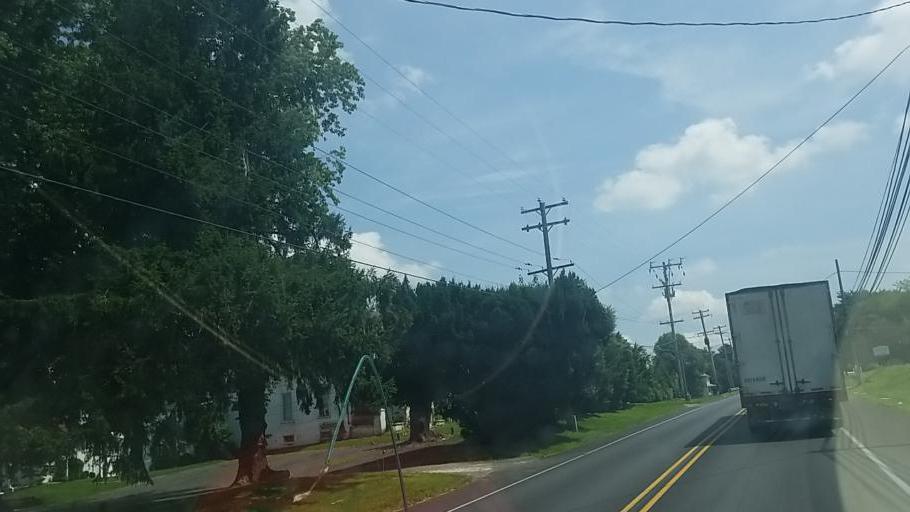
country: US
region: Pennsylvania
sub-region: Chester County
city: Avondale
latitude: 39.8179
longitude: -75.7712
